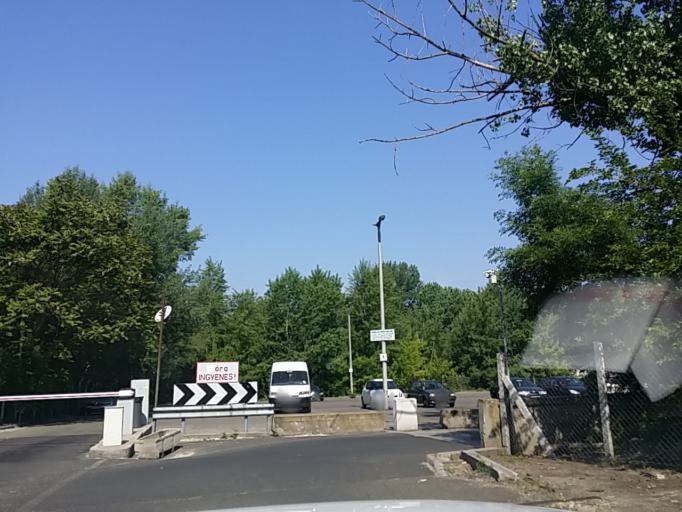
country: HU
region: Budapest
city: Budapest IV. keruelet
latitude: 47.5511
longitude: 19.0724
